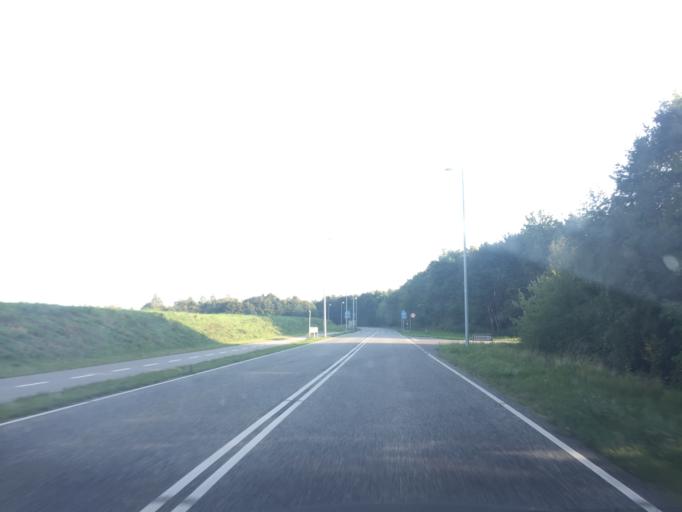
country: DK
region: Zealand
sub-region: Kalundborg Kommune
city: Svebolle
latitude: 55.6148
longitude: 11.2233
